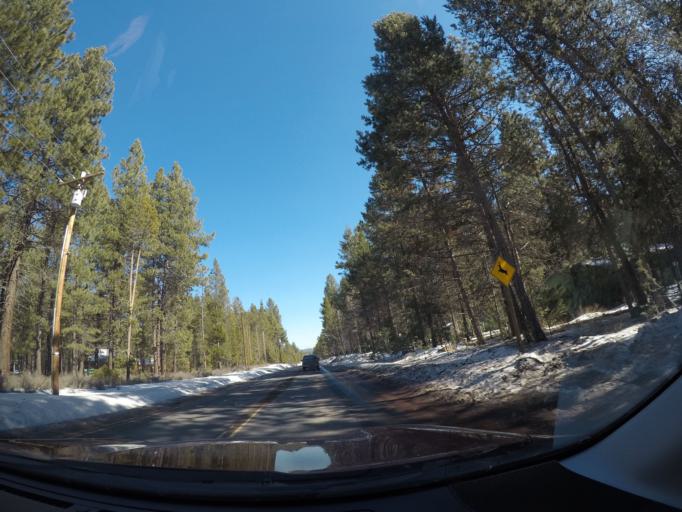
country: US
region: Oregon
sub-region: Deschutes County
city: Sunriver
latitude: 43.8629
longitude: -121.4749
